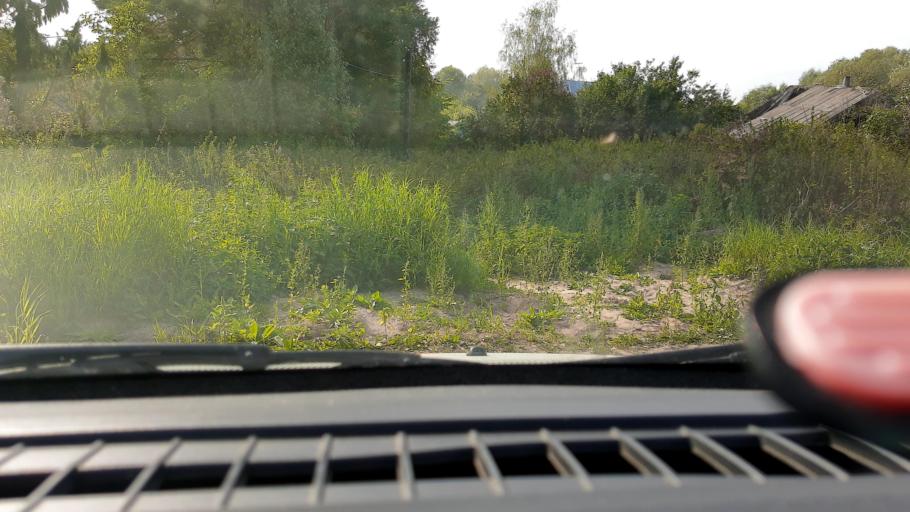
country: RU
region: Nizjnij Novgorod
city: Kstovo
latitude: 55.9961
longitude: 44.2274
